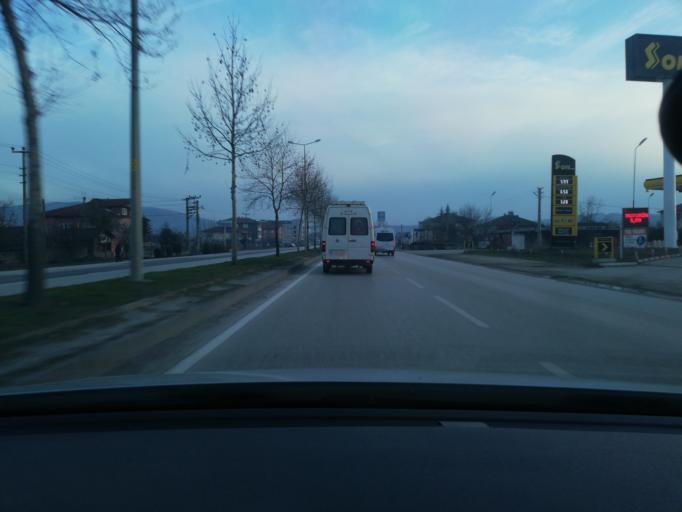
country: TR
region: Duzce
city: Duzce
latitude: 40.8684
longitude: 31.1685
